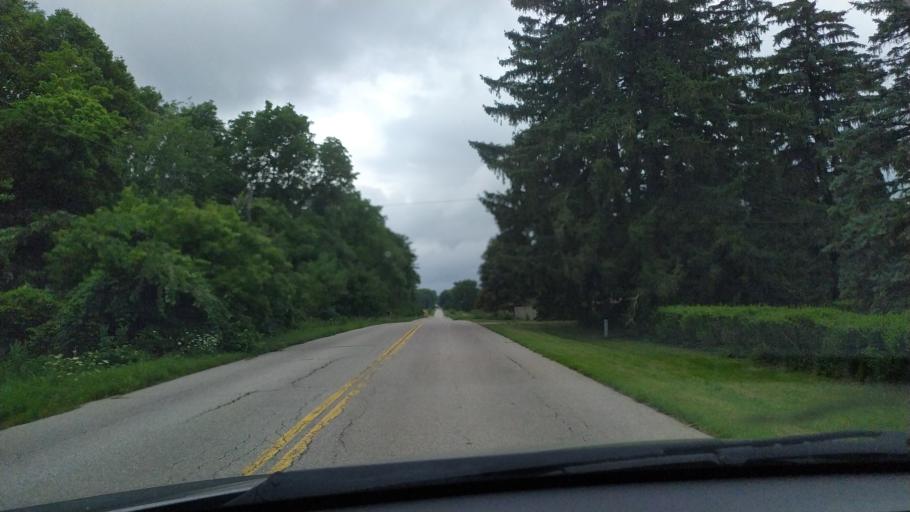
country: CA
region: Ontario
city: Kitchener
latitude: 43.3303
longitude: -80.6610
